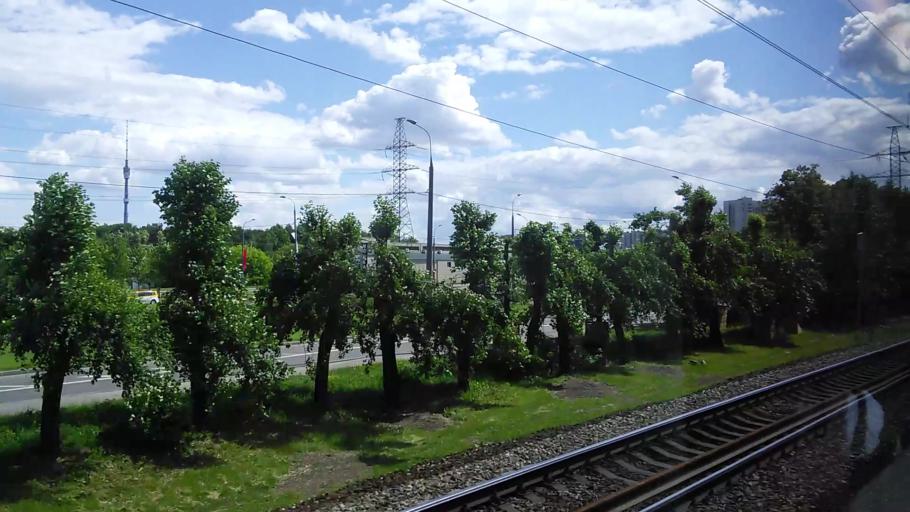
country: RU
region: Moscow
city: Novovladykino
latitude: 55.8373
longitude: 37.5787
